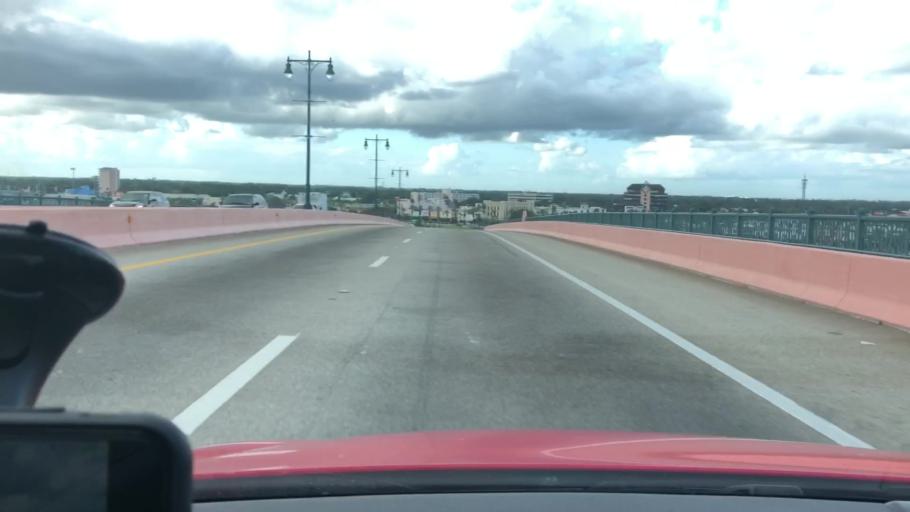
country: US
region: Florida
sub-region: Volusia County
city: Daytona Beach
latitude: 29.2156
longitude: -81.0160
